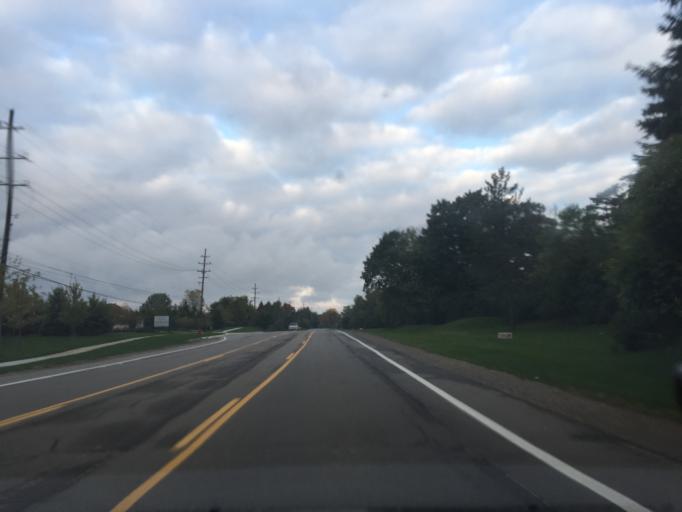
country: US
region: Michigan
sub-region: Oakland County
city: Sylvan Lake
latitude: 42.5807
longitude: -83.3094
